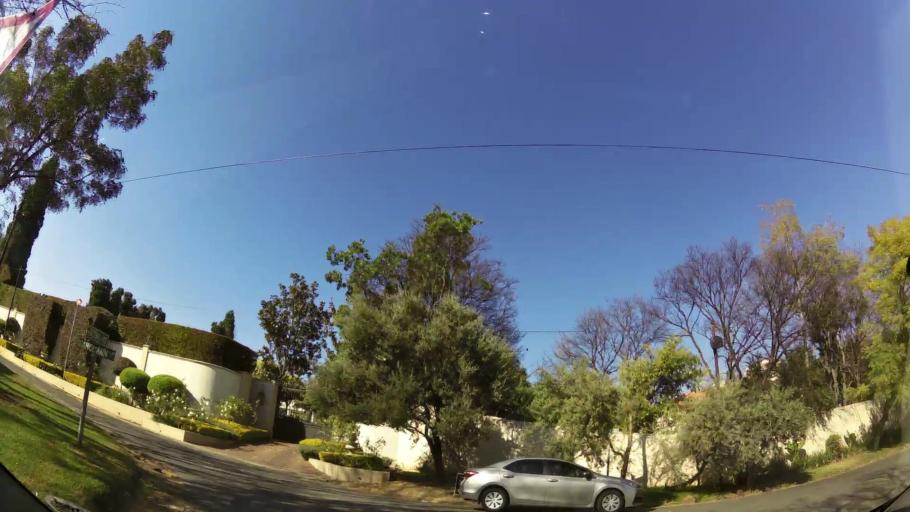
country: ZA
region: Gauteng
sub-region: City of Johannesburg Metropolitan Municipality
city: Modderfontein
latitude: -26.0732
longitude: 28.0576
